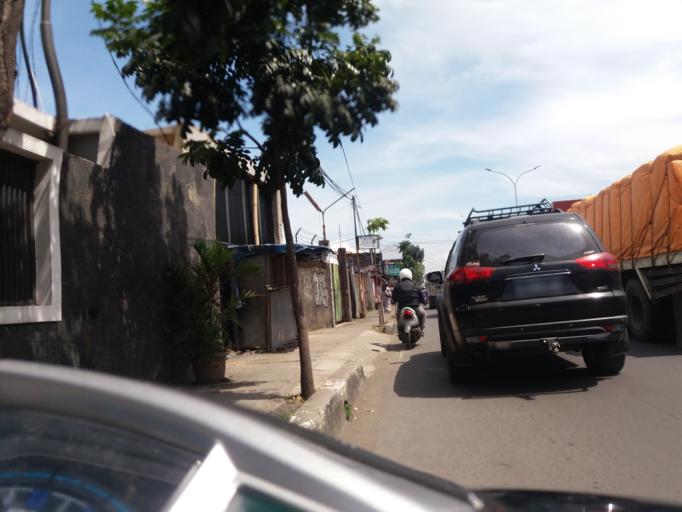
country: ID
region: West Java
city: Bandung
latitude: -6.9462
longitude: 107.6396
